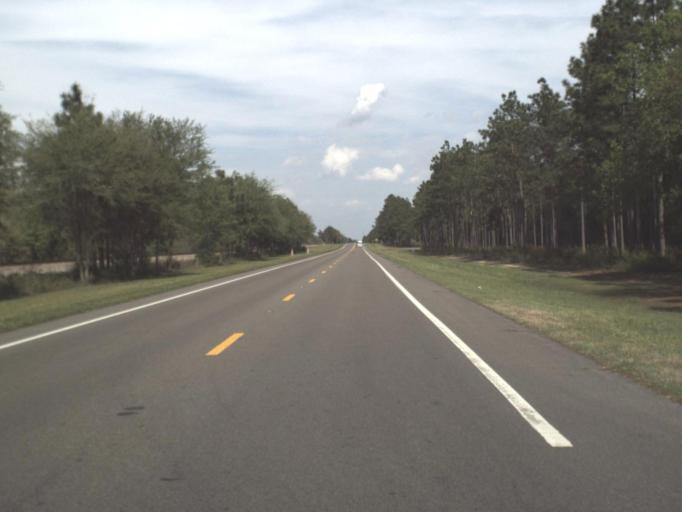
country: US
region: Florida
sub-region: Santa Rosa County
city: East Milton
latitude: 30.6469
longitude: -86.9200
